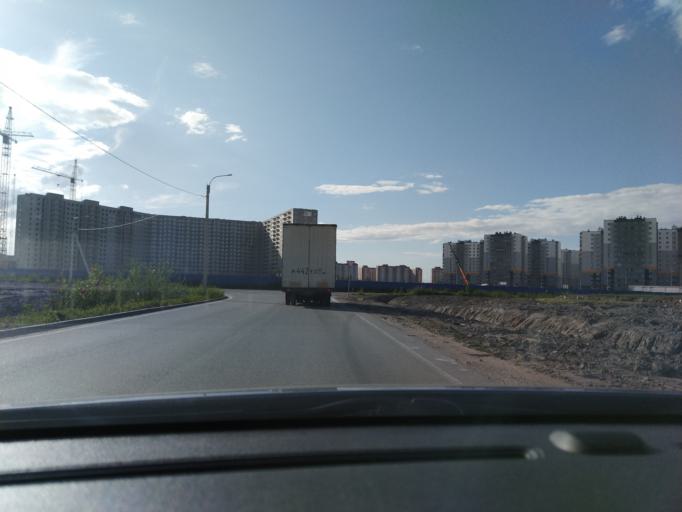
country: RU
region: St.-Petersburg
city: Gorelovo
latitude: 59.7853
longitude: 30.1674
